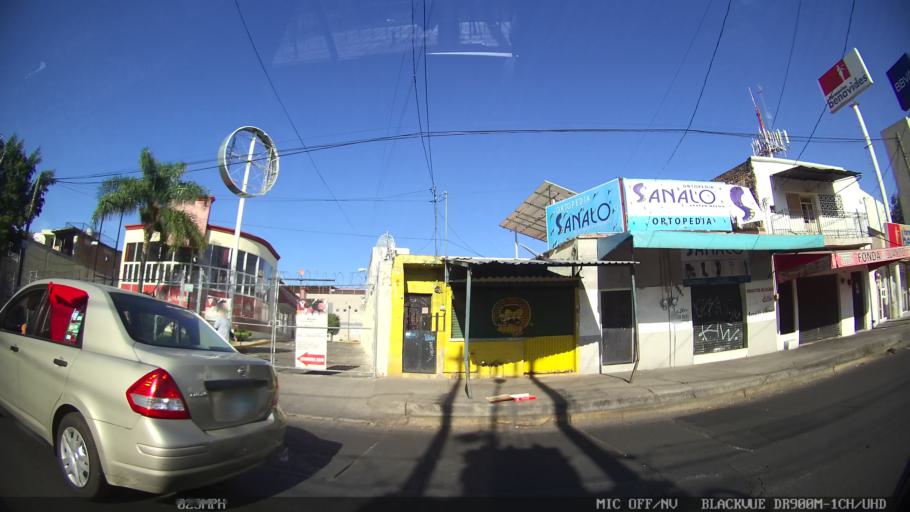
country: MX
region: Jalisco
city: Tlaquepaque
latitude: 20.6864
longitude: -103.3258
